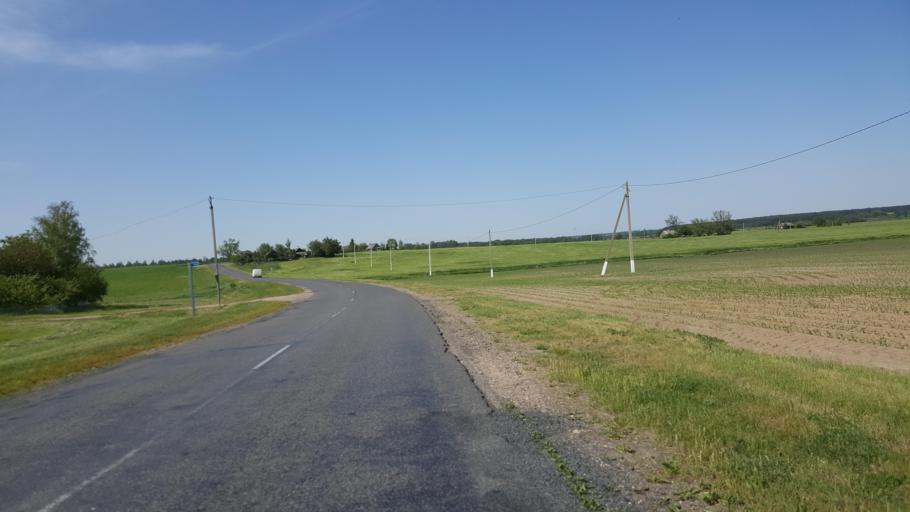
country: BY
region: Brest
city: Charnawchytsy
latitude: 52.2982
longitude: 23.6067
